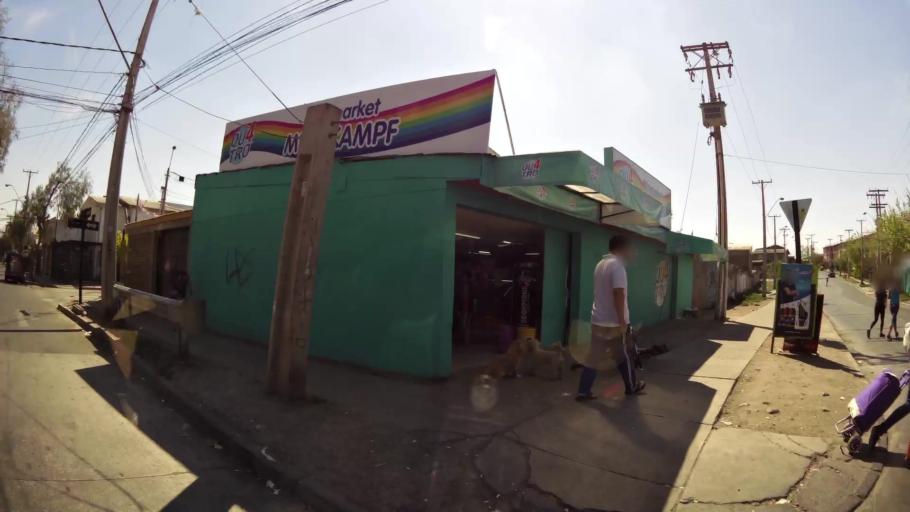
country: CL
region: Santiago Metropolitan
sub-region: Provincia de Cordillera
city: Puente Alto
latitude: -33.6286
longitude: -70.6075
